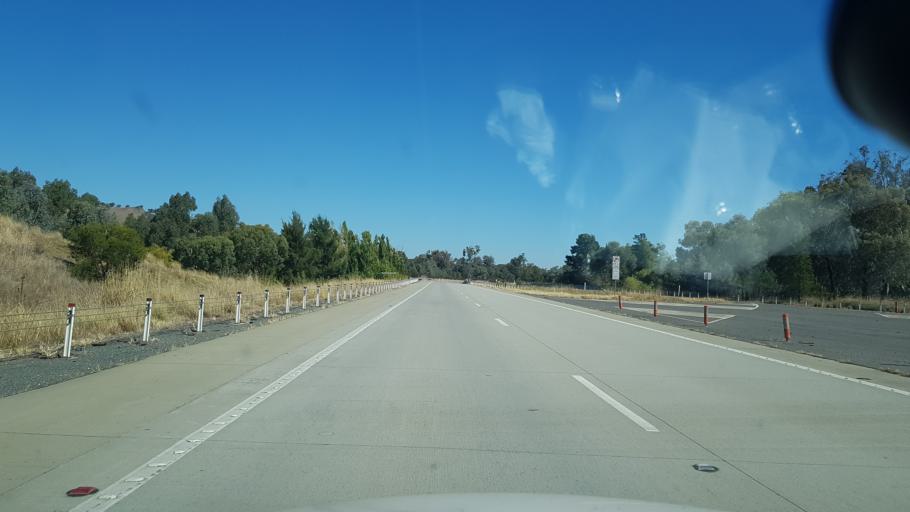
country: AU
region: New South Wales
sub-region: Greater Hume Shire
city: Holbrook
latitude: -35.8992
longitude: 147.1662
